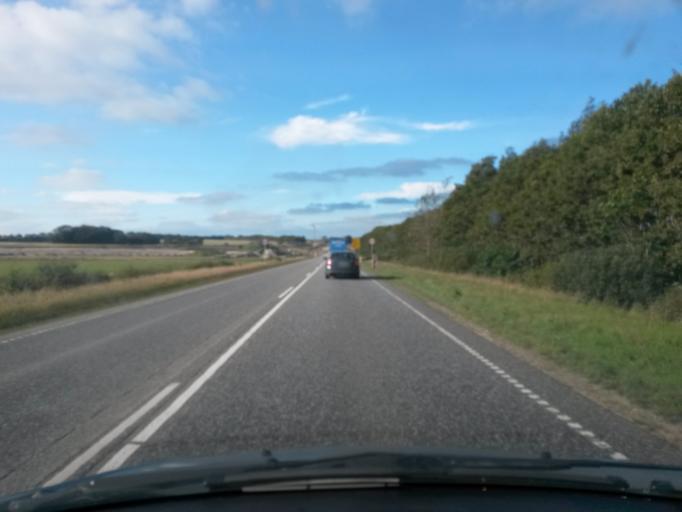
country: DK
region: Central Jutland
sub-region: Herning Kommune
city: Avlum
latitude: 56.2896
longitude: 8.7362
